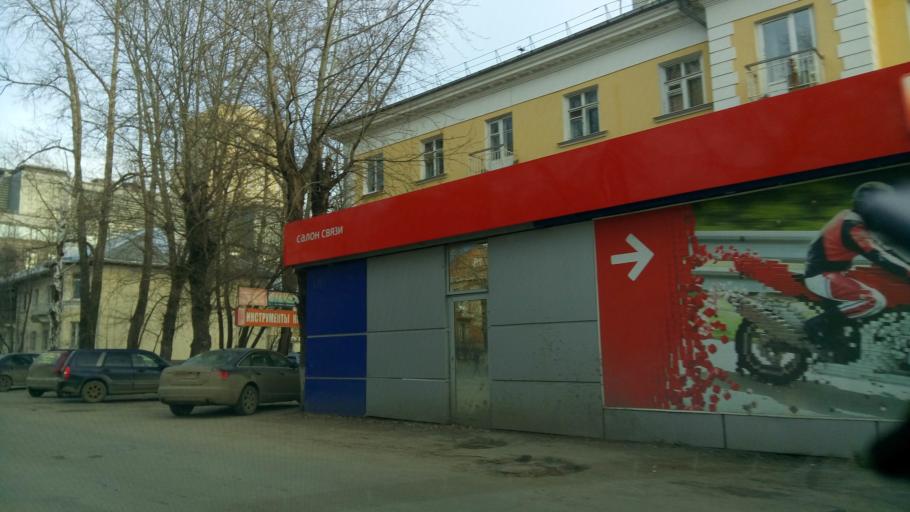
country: RU
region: Sverdlovsk
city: Shuvakish
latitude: 56.8719
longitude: 60.5206
